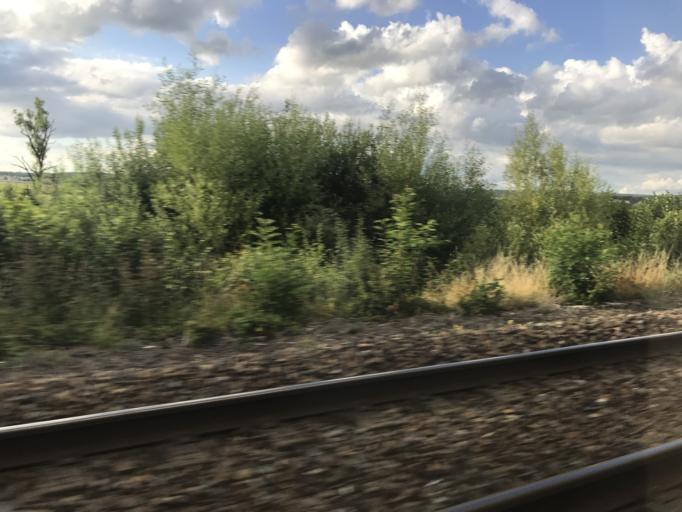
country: FR
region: Champagne-Ardenne
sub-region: Departement des Ardennes
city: Donchery
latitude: 49.6996
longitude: 4.8863
